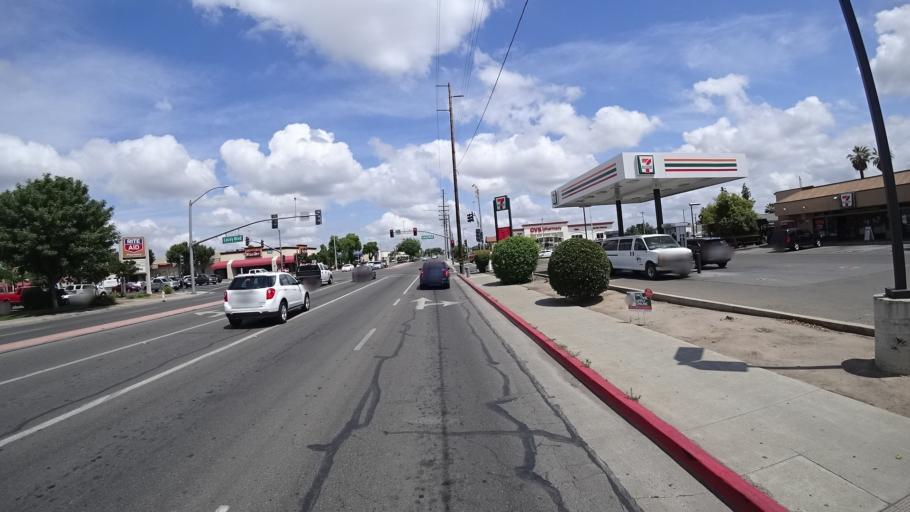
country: US
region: California
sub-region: Kings County
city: Hanford
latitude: 36.3276
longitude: -119.6550
